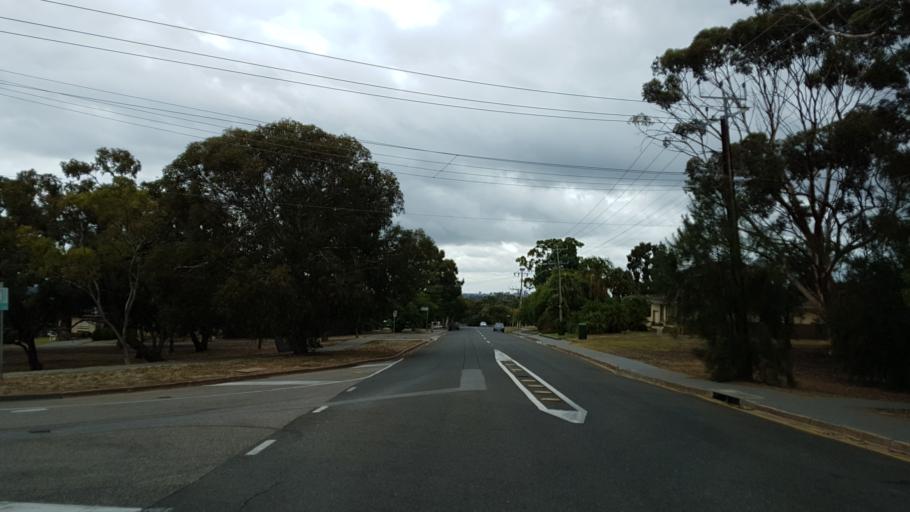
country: AU
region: South Australia
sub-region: Mitcham
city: Clapham
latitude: -35.0036
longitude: 138.5935
